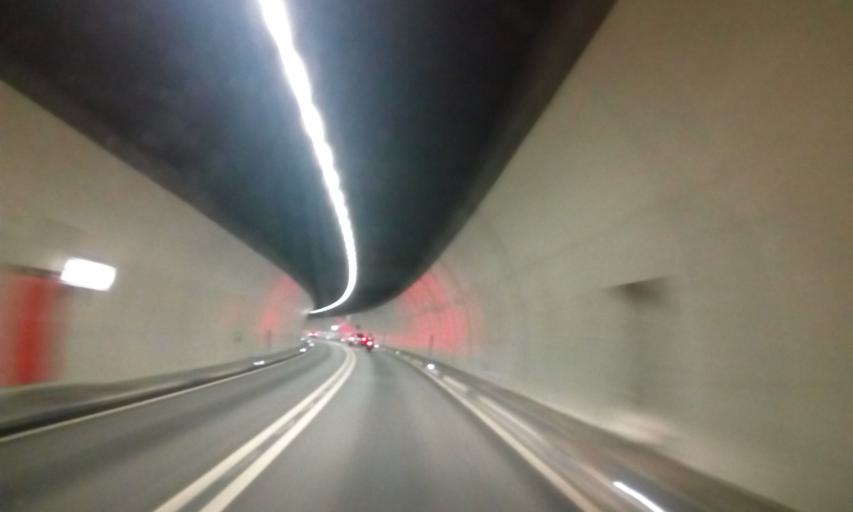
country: CH
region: Grisons
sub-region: Imboden District
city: Bonaduz
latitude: 46.8285
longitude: 9.3626
